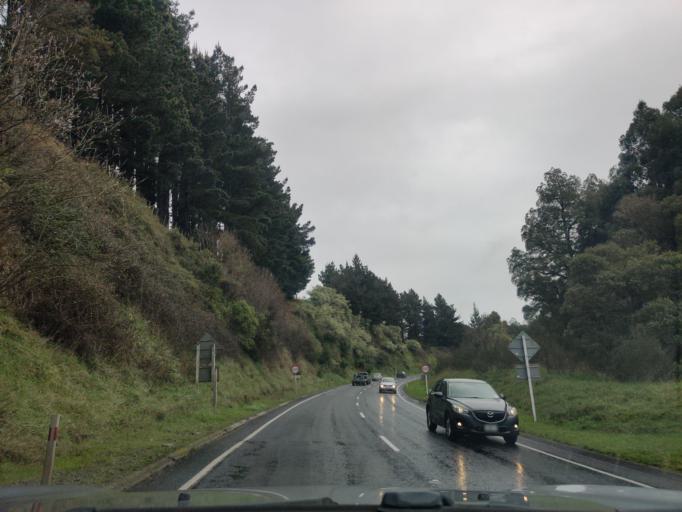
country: NZ
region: Manawatu-Wanganui
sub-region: Palmerston North City
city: Palmerston North
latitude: -40.0541
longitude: 176.2384
